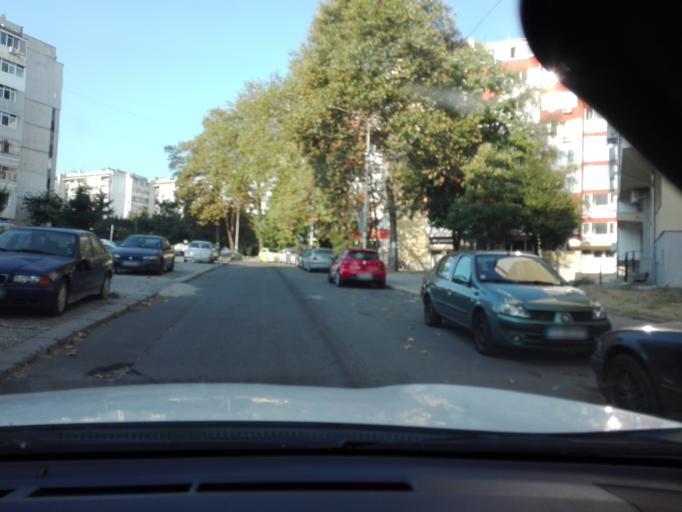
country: BG
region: Burgas
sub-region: Obshtina Burgas
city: Burgas
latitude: 42.4644
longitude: 27.4162
